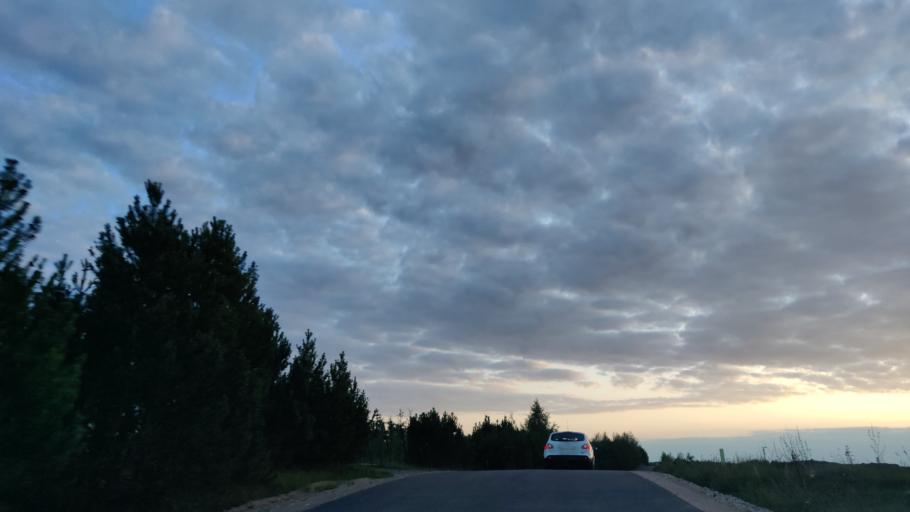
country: LT
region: Vilnius County
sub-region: Trakai
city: Rudiskes
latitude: 54.6086
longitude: 24.8069
